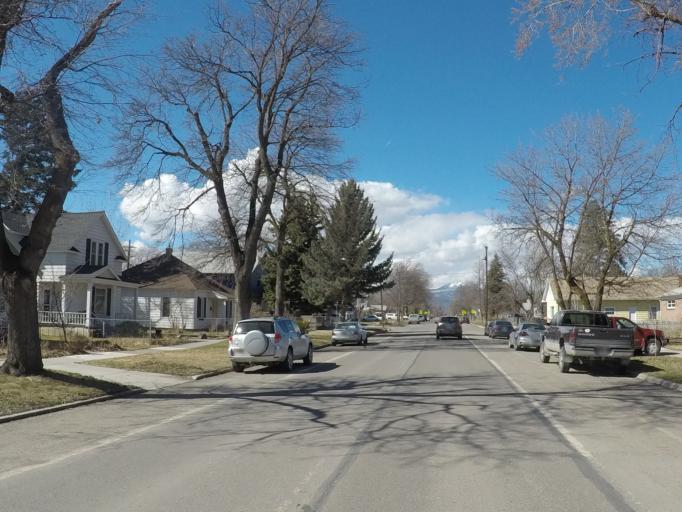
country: US
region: Montana
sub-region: Missoula County
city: Missoula
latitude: 46.8651
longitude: -114.0085
